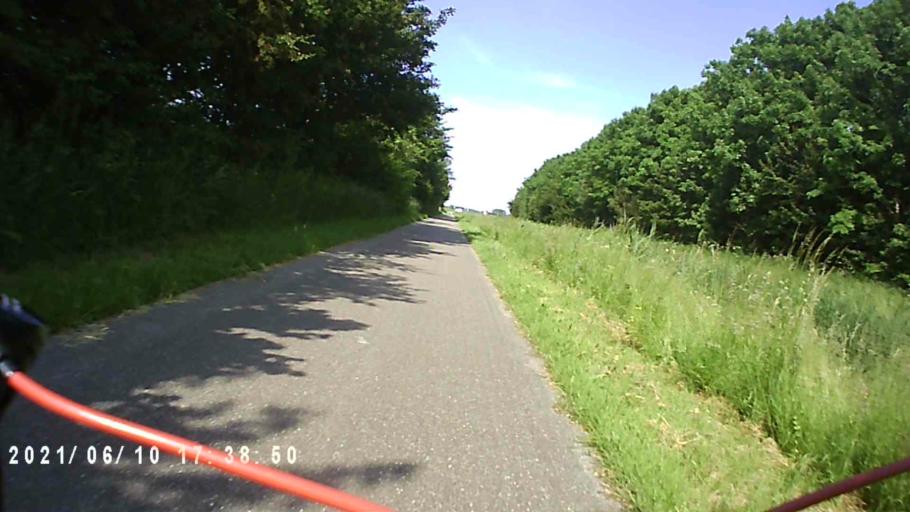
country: NL
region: Groningen
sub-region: Gemeente De Marne
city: Ulrum
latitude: 53.3254
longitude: 6.2804
